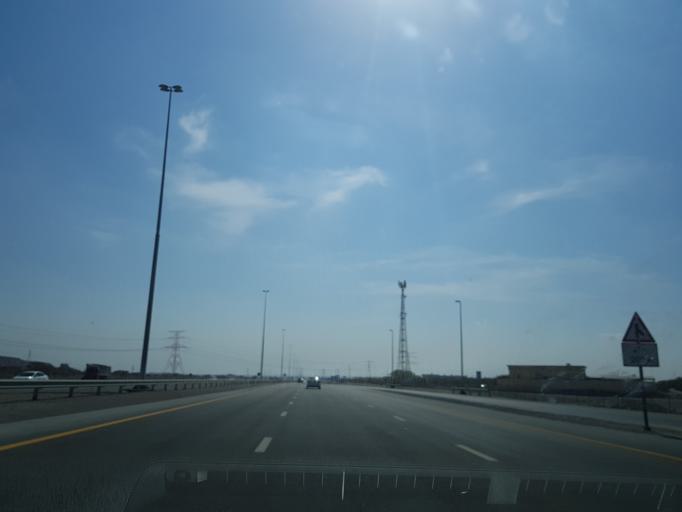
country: AE
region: Ra's al Khaymah
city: Ras al-Khaimah
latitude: 25.7725
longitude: 56.0277
